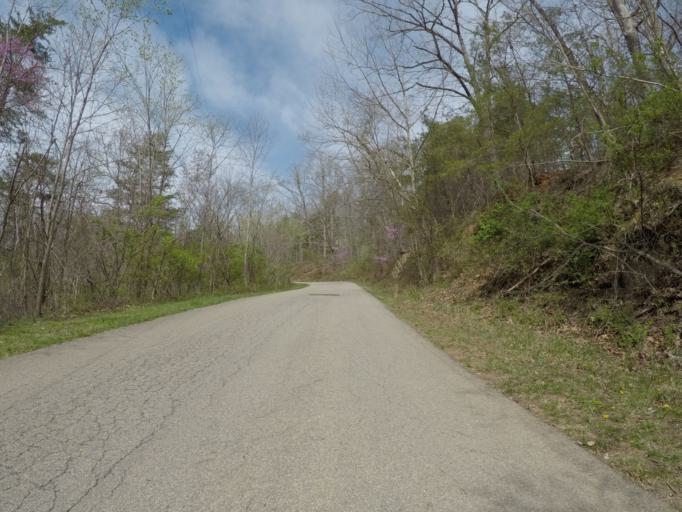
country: US
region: West Virginia
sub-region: Wayne County
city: Lavalette
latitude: 38.3480
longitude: -82.3947
